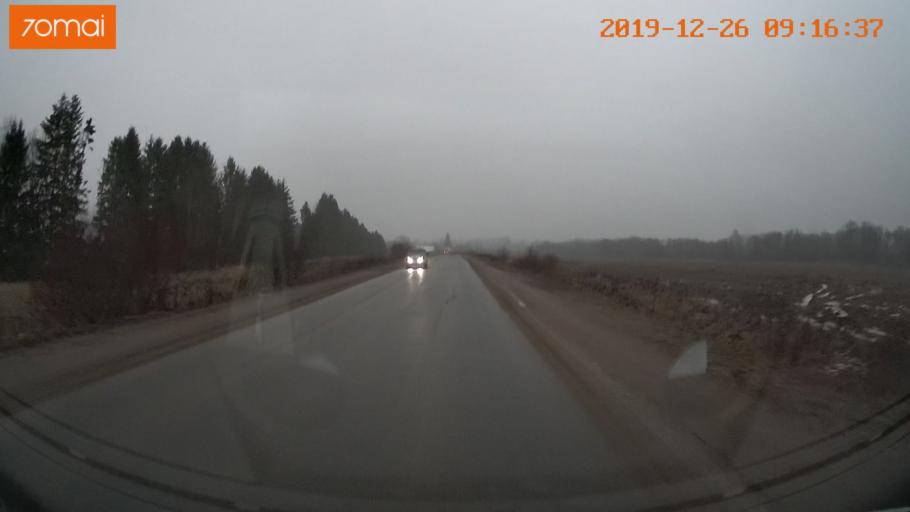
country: RU
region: Vologda
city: Gryazovets
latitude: 58.9206
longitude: 40.2391
